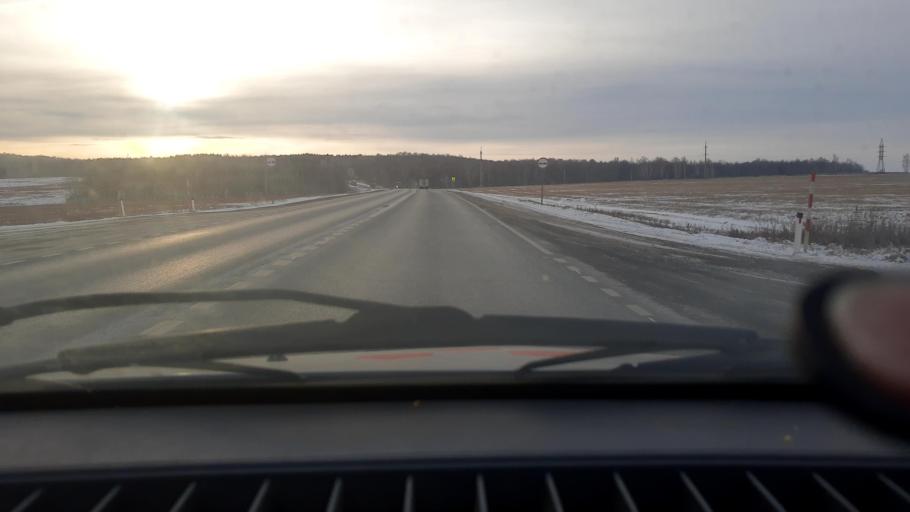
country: RU
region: Bashkortostan
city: Avdon
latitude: 54.8548
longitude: 55.7033
